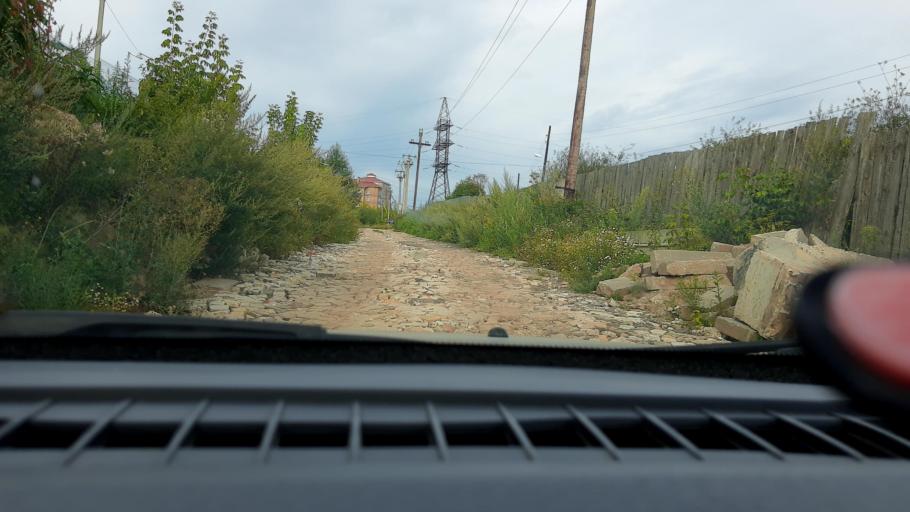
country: RU
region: Nizjnij Novgorod
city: Afonino
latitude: 56.2803
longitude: 44.0765
